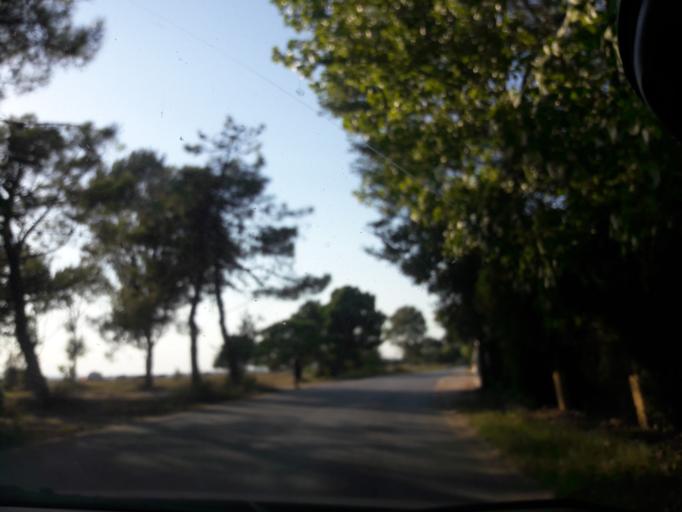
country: GR
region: Central Macedonia
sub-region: Nomos Chalkidikis
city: Nea Kallikrateia
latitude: 40.3361
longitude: 23.0209
